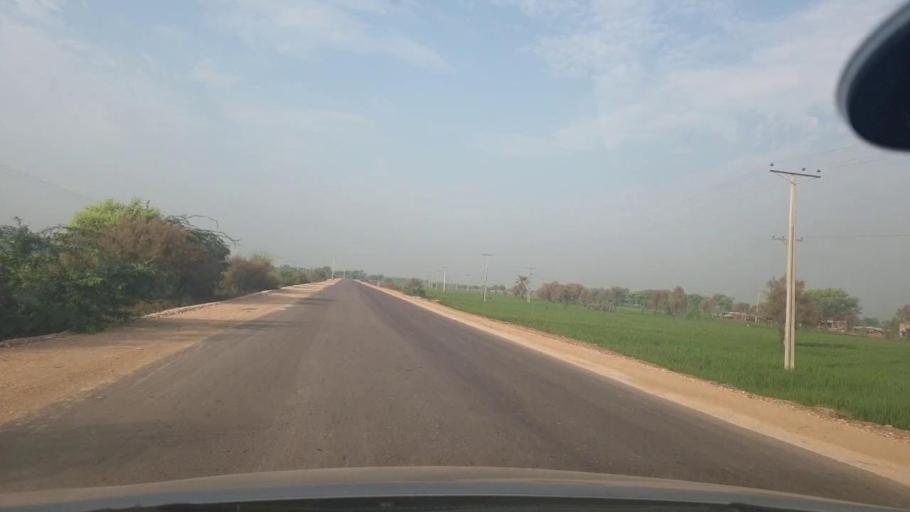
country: PK
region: Sindh
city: Jacobabad
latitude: 28.2504
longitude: 68.4041
